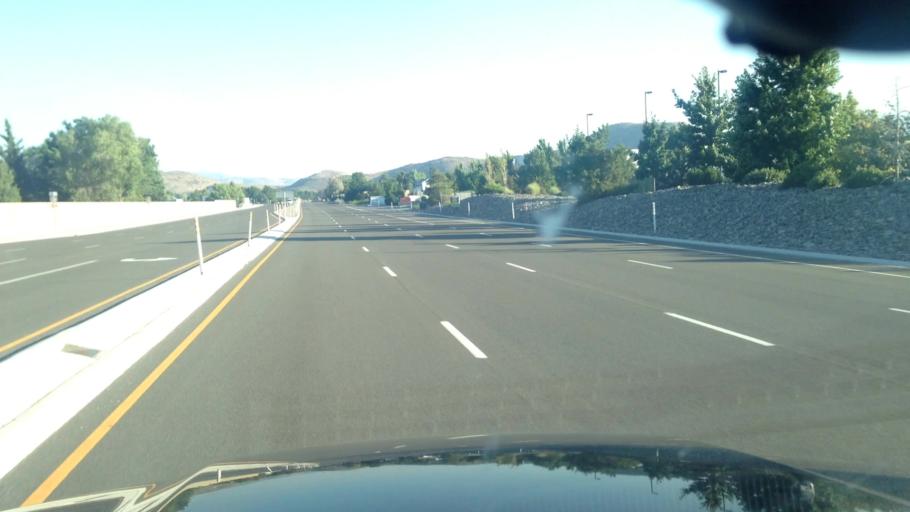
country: US
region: Nevada
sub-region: Washoe County
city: Sparks
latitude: 39.4966
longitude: -119.7481
